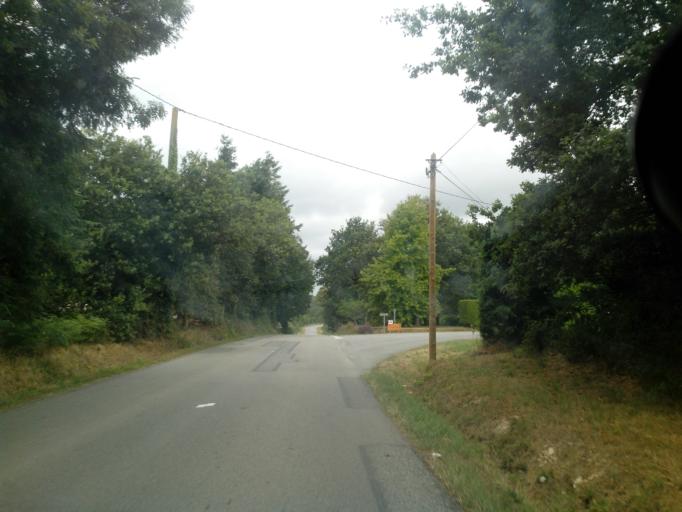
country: FR
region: Brittany
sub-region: Departement du Morbihan
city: Merlevenez
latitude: 47.7391
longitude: -3.2712
